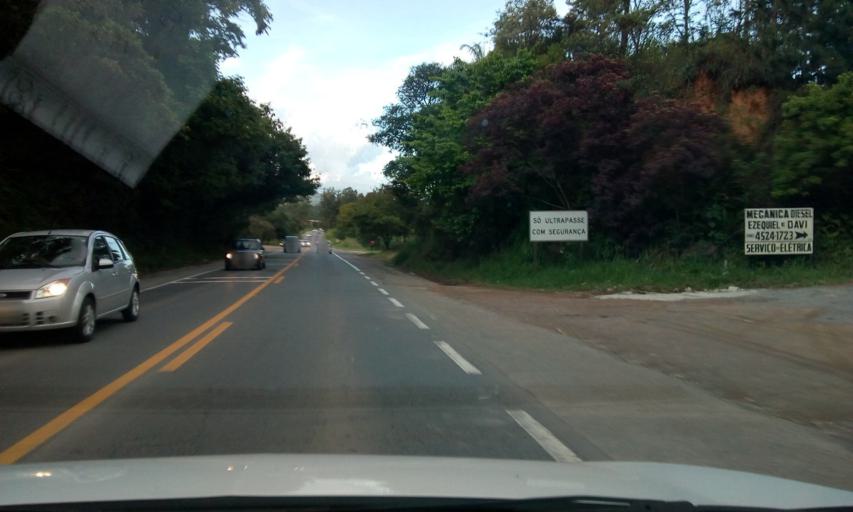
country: BR
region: Sao Paulo
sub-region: Itatiba
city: Itatiba
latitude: -22.9995
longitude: -46.8083
